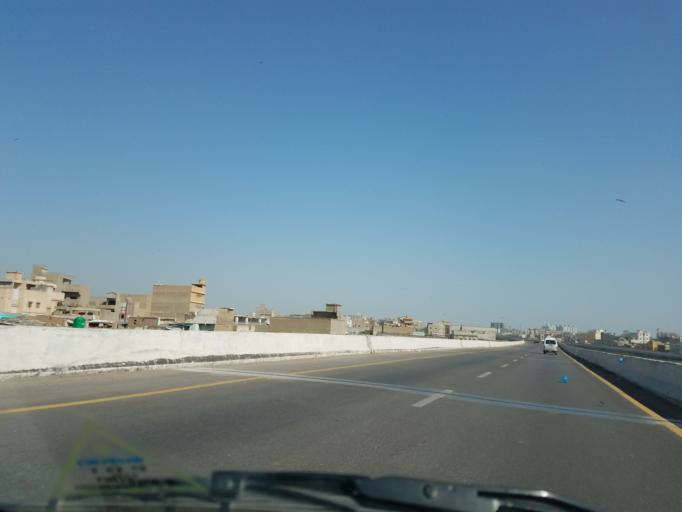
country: PK
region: Sindh
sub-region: Karachi District
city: Karachi
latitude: 24.8814
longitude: 67.0067
